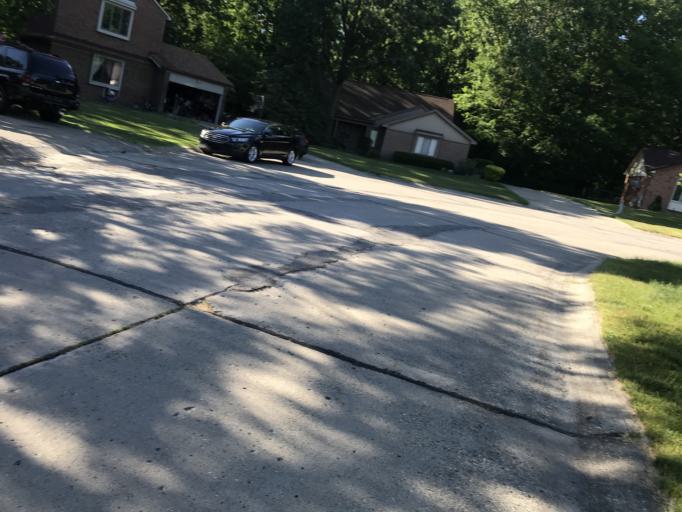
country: US
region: Michigan
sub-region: Oakland County
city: Farmington Hills
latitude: 42.4761
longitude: -83.3470
